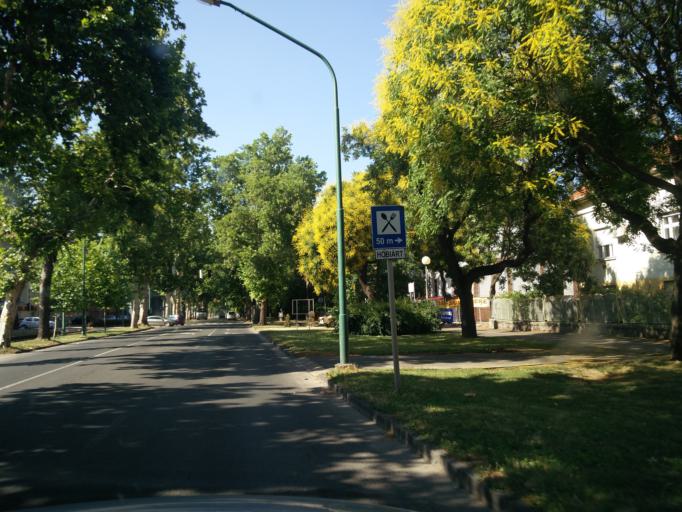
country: HU
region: Csongrad
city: Szeged
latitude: 46.2637
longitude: 20.1577
